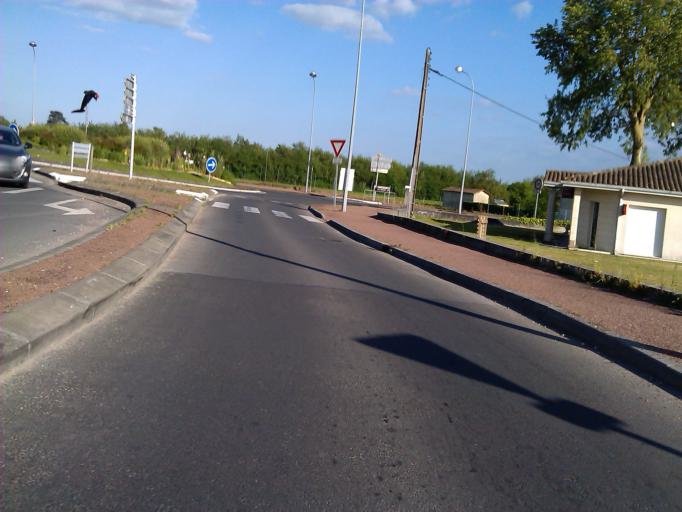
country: FR
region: Aquitaine
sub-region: Departement de la Gironde
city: Cubzac-les-Ponts
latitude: 44.9878
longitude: -0.4501
